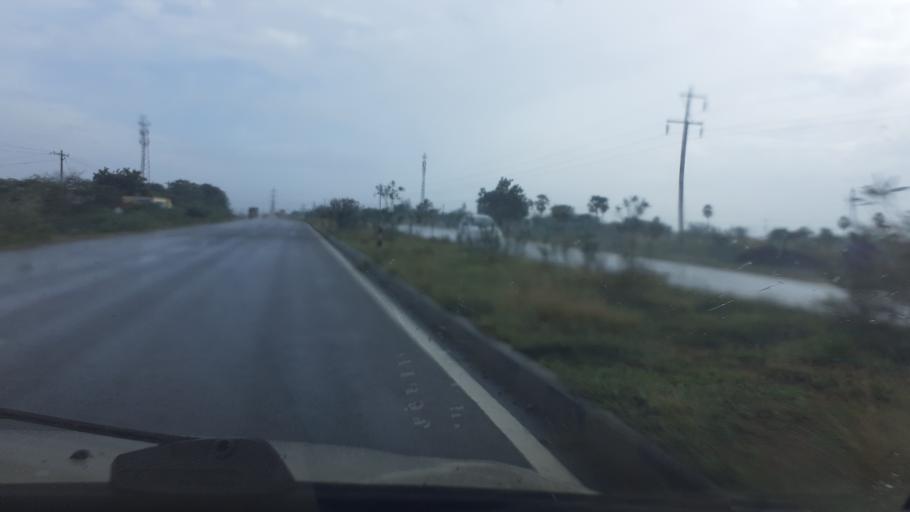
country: IN
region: Tamil Nadu
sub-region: Tirunelveli Kattabo
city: Gangaikondan
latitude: 8.8999
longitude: 77.7648
